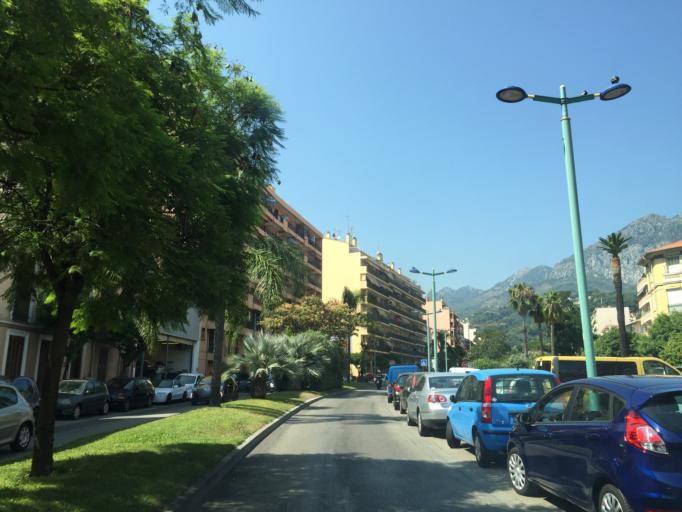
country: FR
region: Provence-Alpes-Cote d'Azur
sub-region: Departement des Alpes-Maritimes
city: Menton
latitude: 43.7785
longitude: 7.4936
